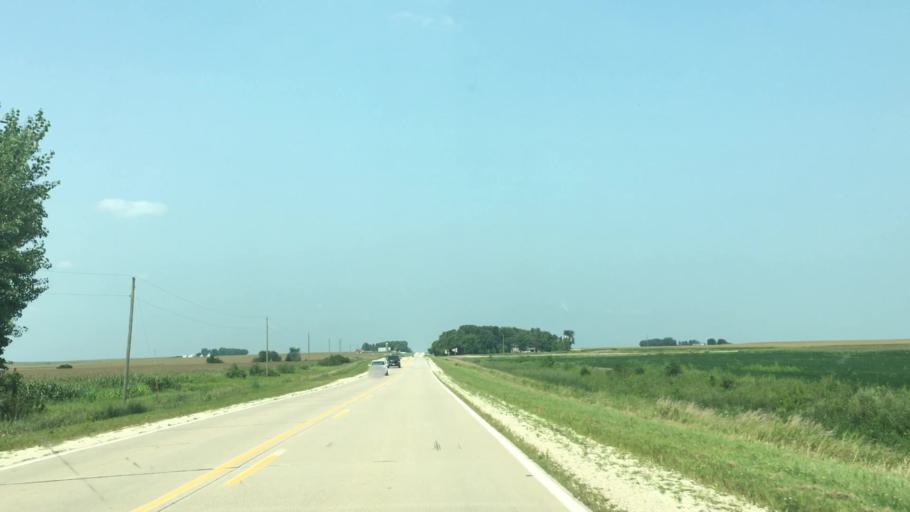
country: US
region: Iowa
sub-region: Fayette County
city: Fayette
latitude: 42.7563
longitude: -91.8043
